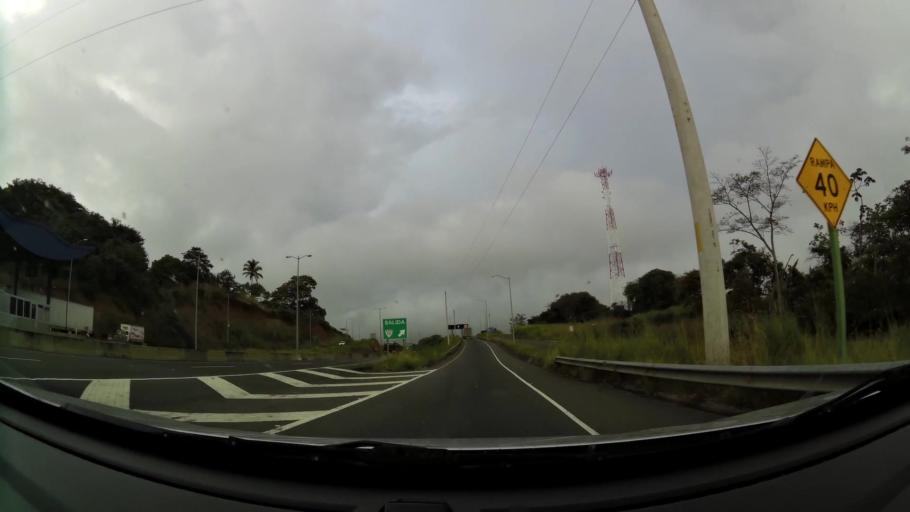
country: CR
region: Heredia
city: Colon
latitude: 9.9647
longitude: -84.2830
